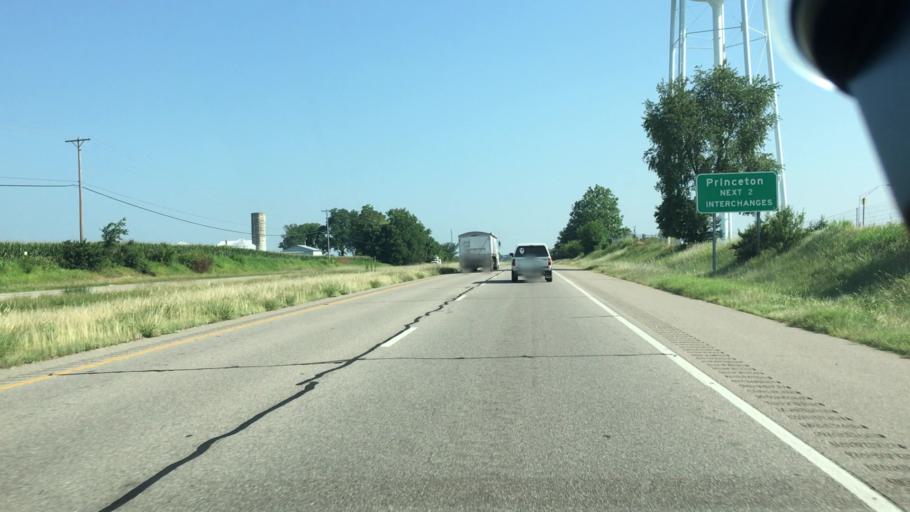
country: US
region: Indiana
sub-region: Gibson County
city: Fort Branch
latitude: 38.2893
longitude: -87.5674
